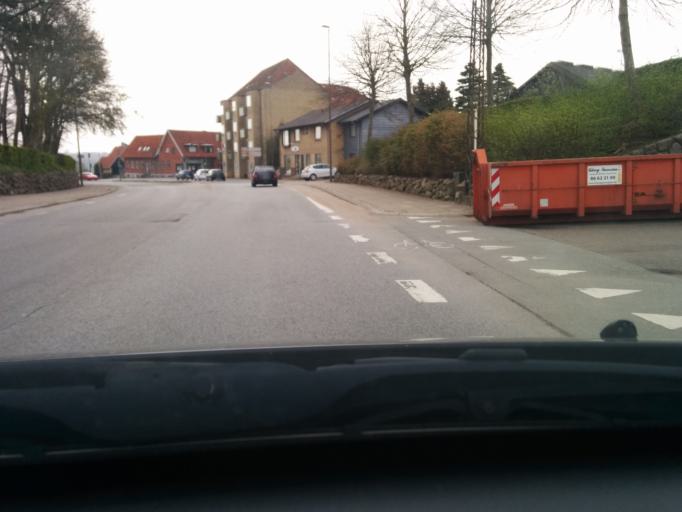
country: DK
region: Central Jutland
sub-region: Viborg Kommune
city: Viborg
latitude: 56.4567
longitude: 9.4114
